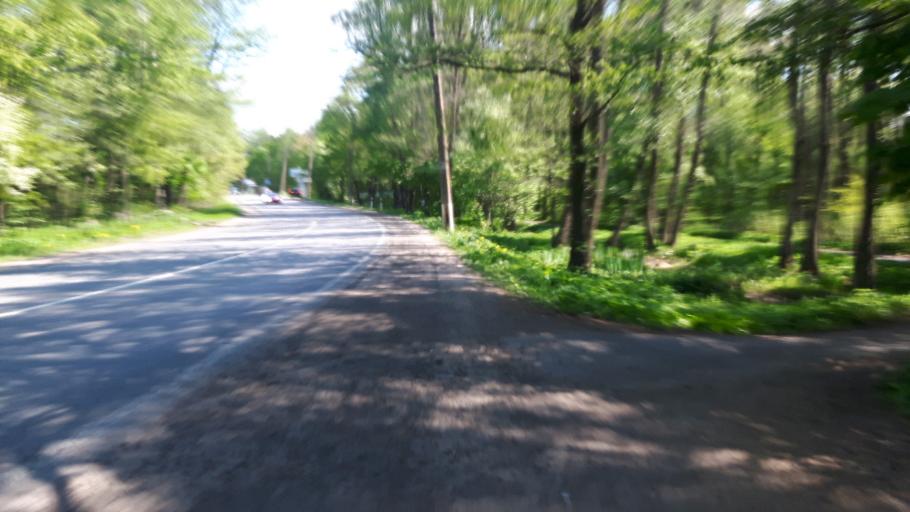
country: RU
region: St.-Petersburg
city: Repino
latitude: 60.1626
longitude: 29.8471
